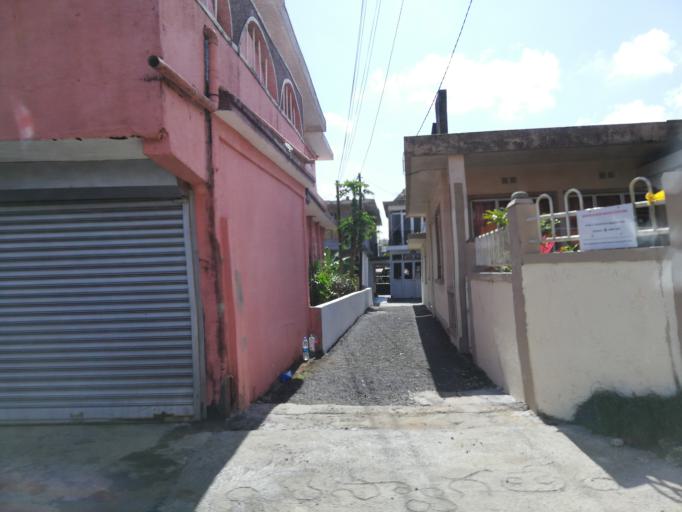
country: MU
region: Moka
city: Verdun
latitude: -20.2193
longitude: 57.5362
